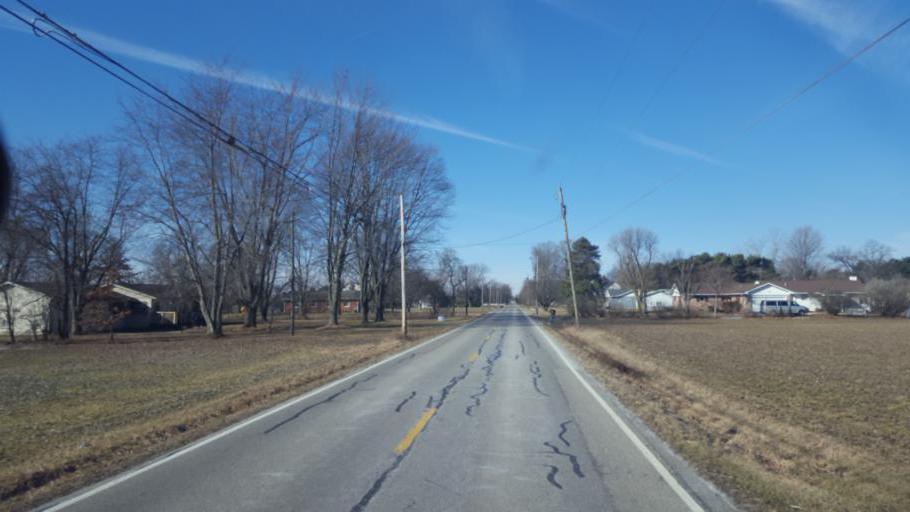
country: US
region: Ohio
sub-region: Marion County
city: Marion
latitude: 40.5348
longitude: -83.1253
